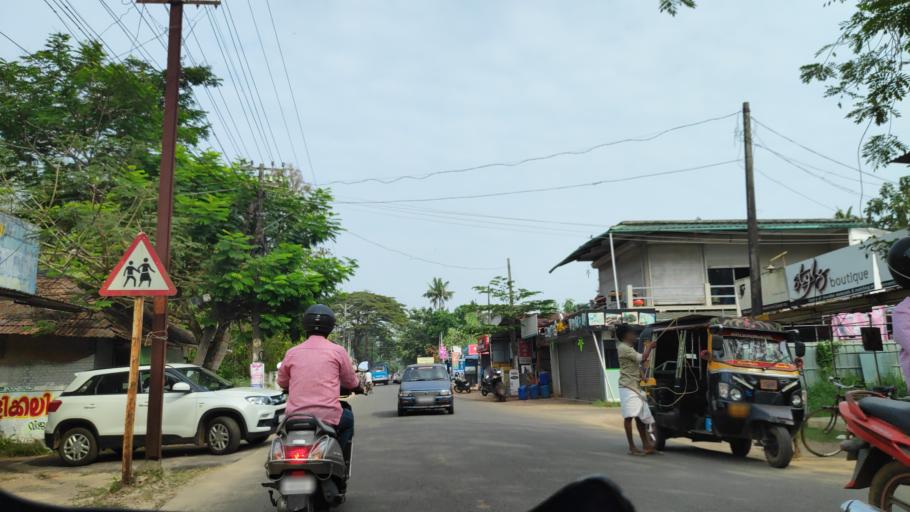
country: IN
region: Kerala
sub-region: Alappuzha
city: Kutiatodu
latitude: 9.7995
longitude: 76.3538
